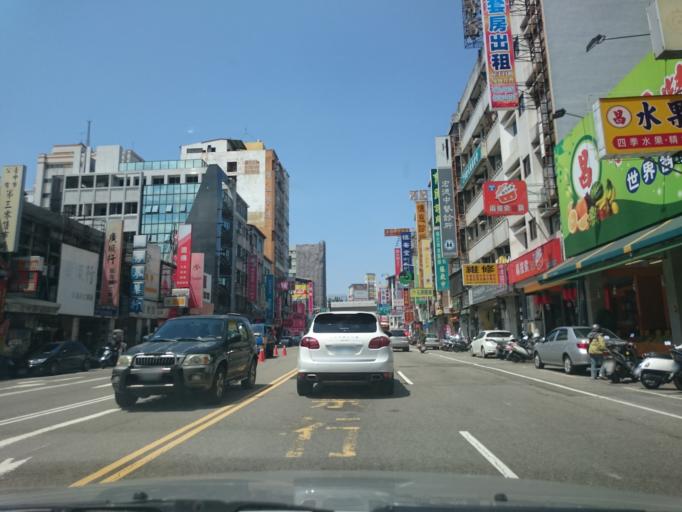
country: TW
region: Taiwan
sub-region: Taichung City
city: Taichung
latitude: 24.1335
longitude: 120.6835
